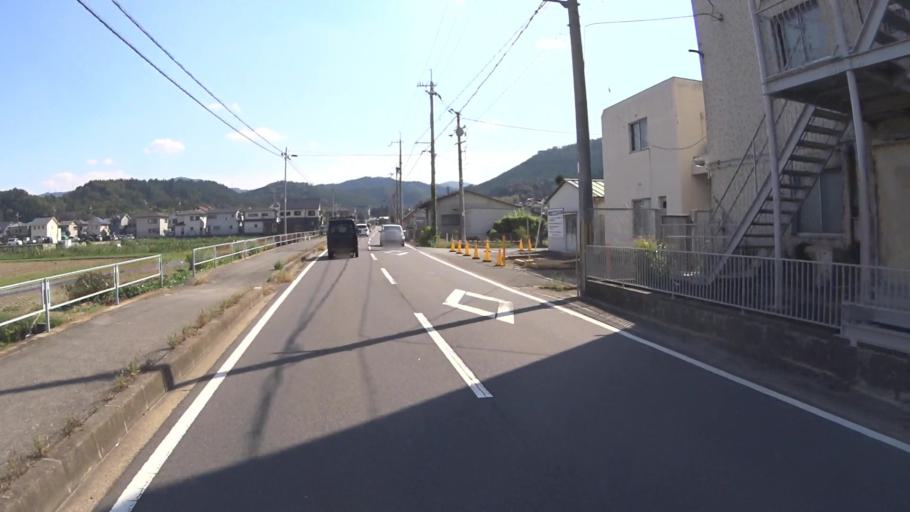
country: JP
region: Kyoto
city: Kameoka
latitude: 35.0022
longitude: 135.5780
